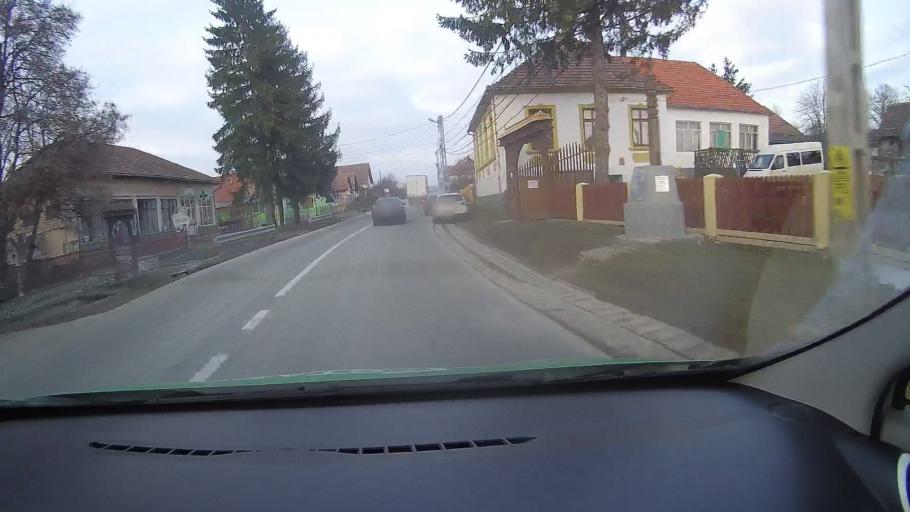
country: RO
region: Harghita
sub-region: Comuna Simonesti
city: Simonesti
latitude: 46.3358
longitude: 25.1076
